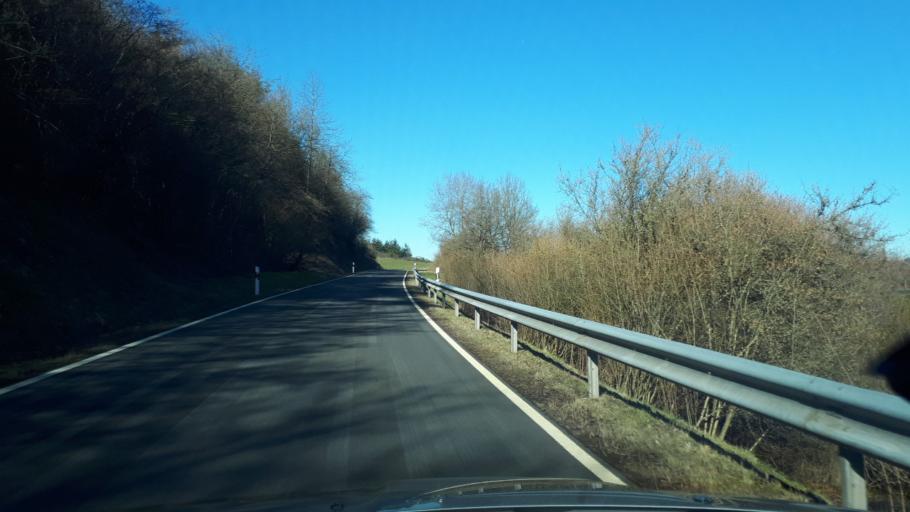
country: DE
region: Rheinland-Pfalz
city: Udler
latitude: 50.1353
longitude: 6.8864
